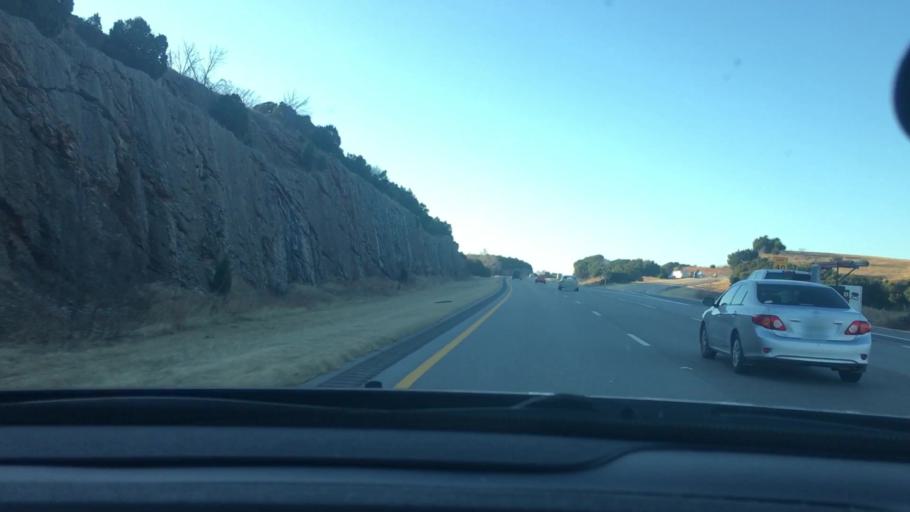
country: US
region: Oklahoma
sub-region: Murray County
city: Davis
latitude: 34.4285
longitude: -97.1335
